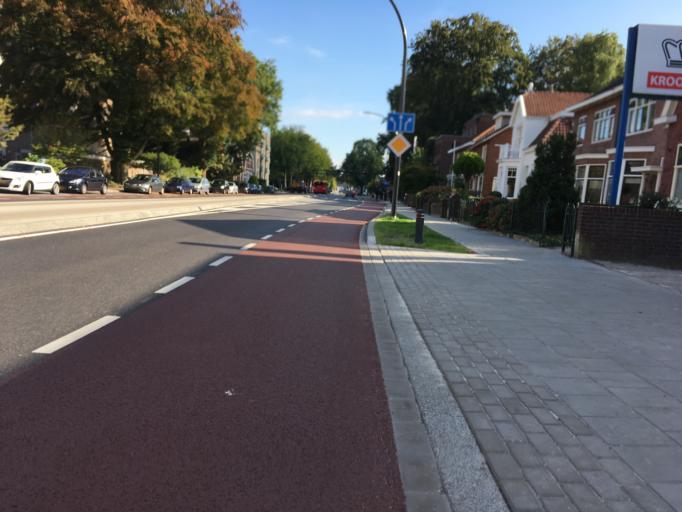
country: NL
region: Overijssel
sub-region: Gemeente Enschede
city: Enschede
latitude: 52.2289
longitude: 6.8737
